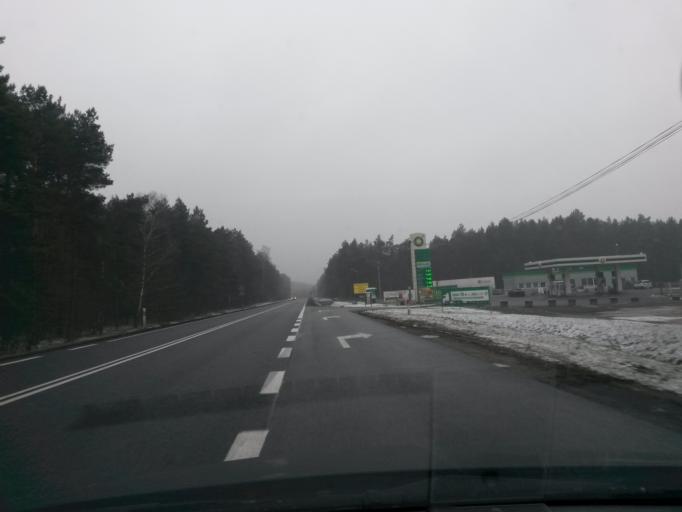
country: PL
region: Kujawsko-Pomorskie
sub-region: Powiat torunski
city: Wielka Nieszawka
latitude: 52.9959
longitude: 18.4660
